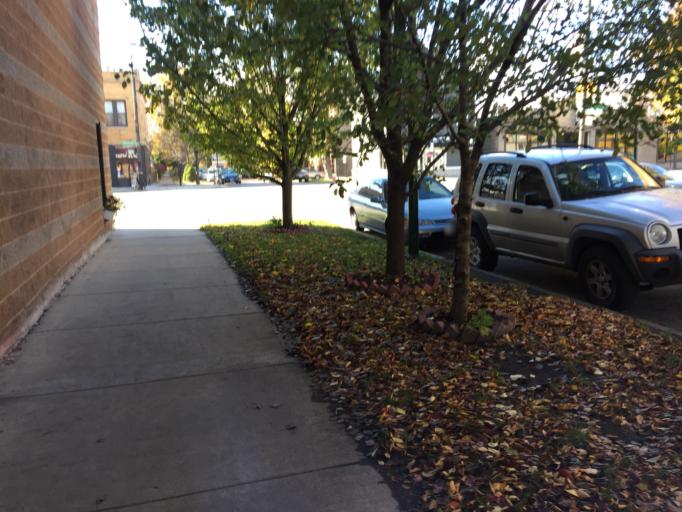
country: US
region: Illinois
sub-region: Cook County
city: Lincolnwood
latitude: 41.9595
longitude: -87.6882
